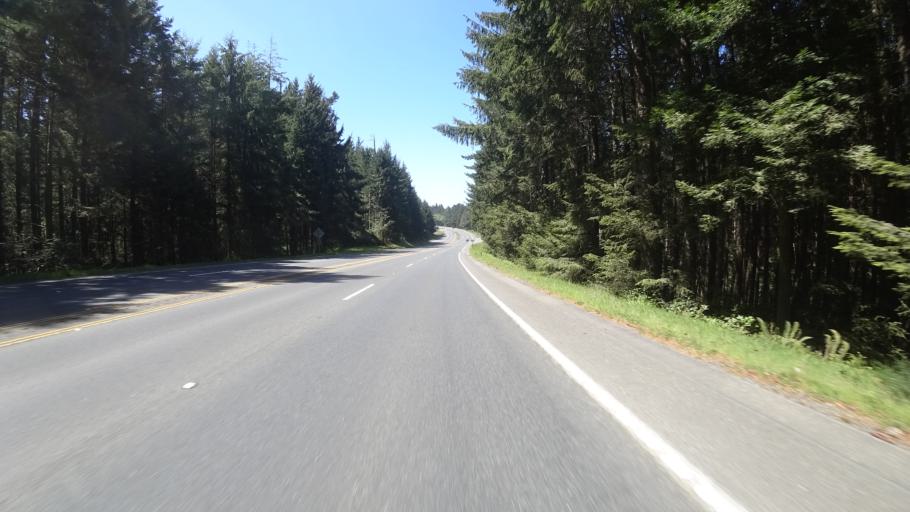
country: US
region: California
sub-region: Humboldt County
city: Westhaven-Moonstone
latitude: 41.1382
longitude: -124.1412
